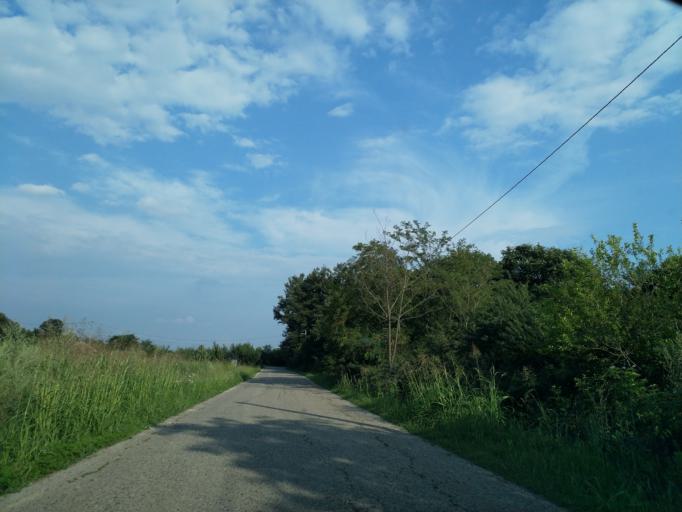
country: RS
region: Central Serbia
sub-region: Pomoravski Okrug
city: Jagodina
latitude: 43.9889
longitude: 21.2104
